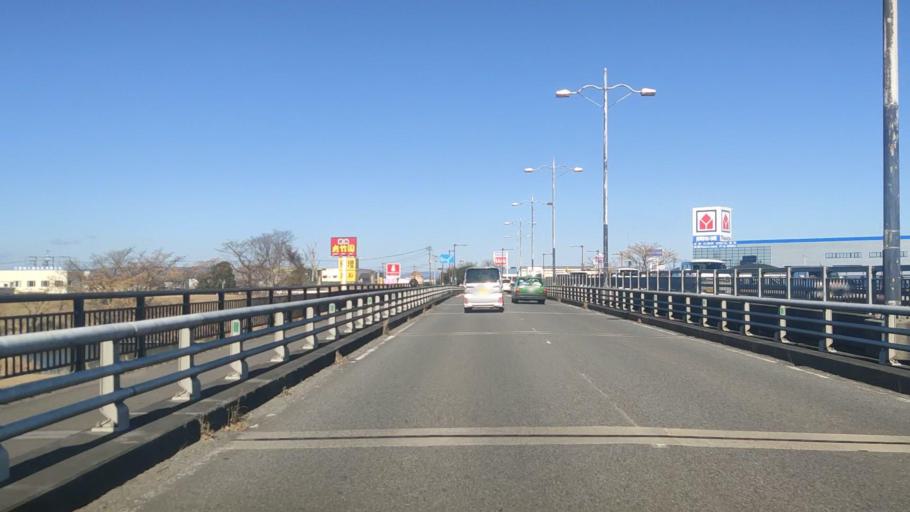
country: JP
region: Miyazaki
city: Miyakonojo
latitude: 31.7496
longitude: 131.0778
